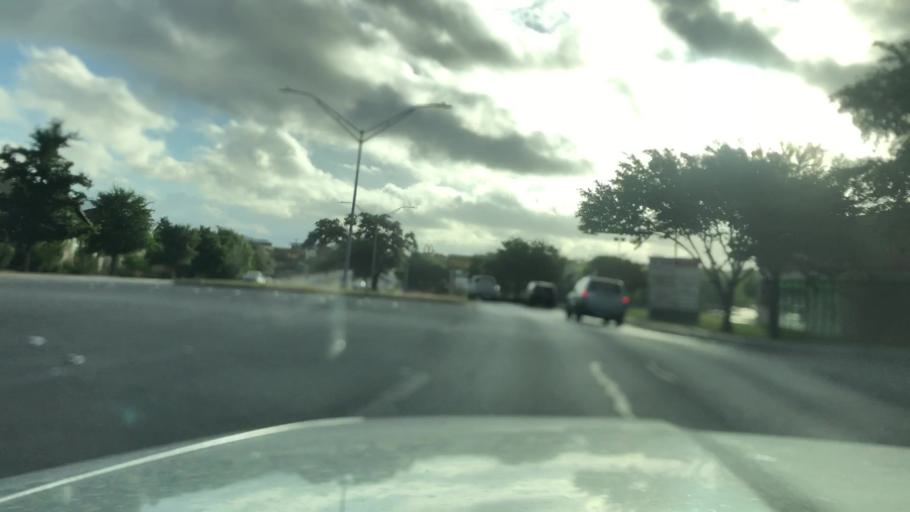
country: US
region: Texas
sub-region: Bexar County
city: Shavano Park
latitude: 29.5729
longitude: -98.5476
